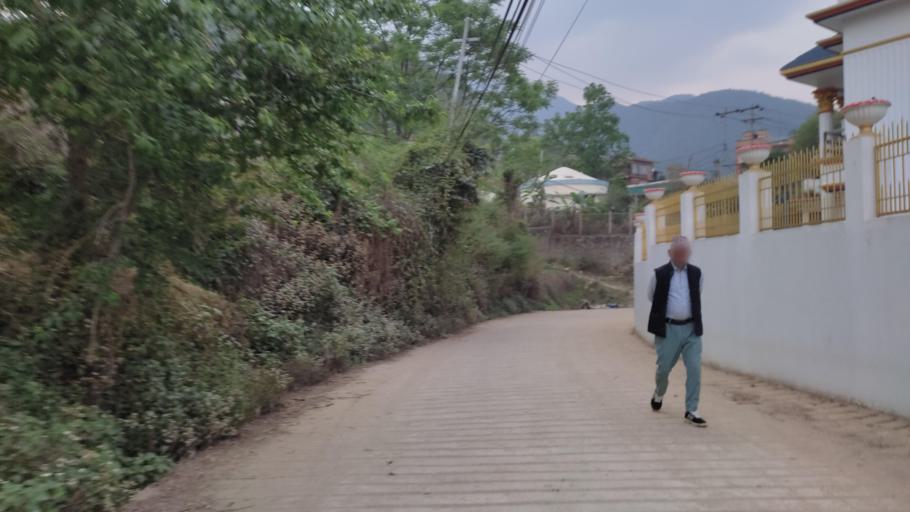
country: NP
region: Central Region
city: Kirtipur
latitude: 27.6732
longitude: 85.2401
